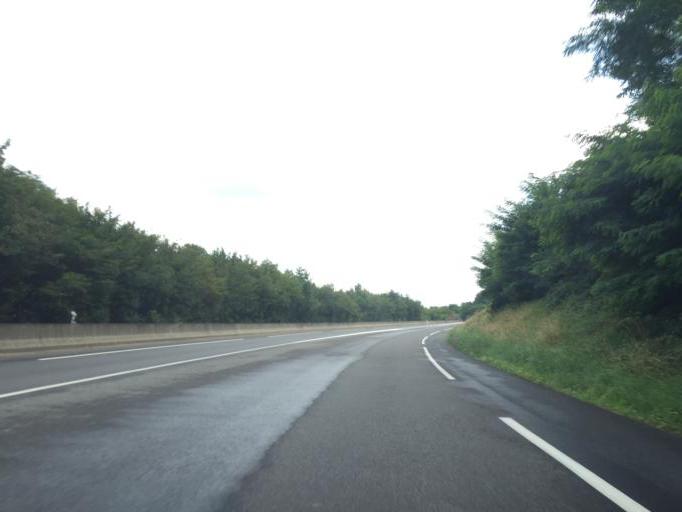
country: FR
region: Rhone-Alpes
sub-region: Departement du Rhone
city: Pontcharra-sur-Turdine
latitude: 45.8734
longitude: 4.4853
